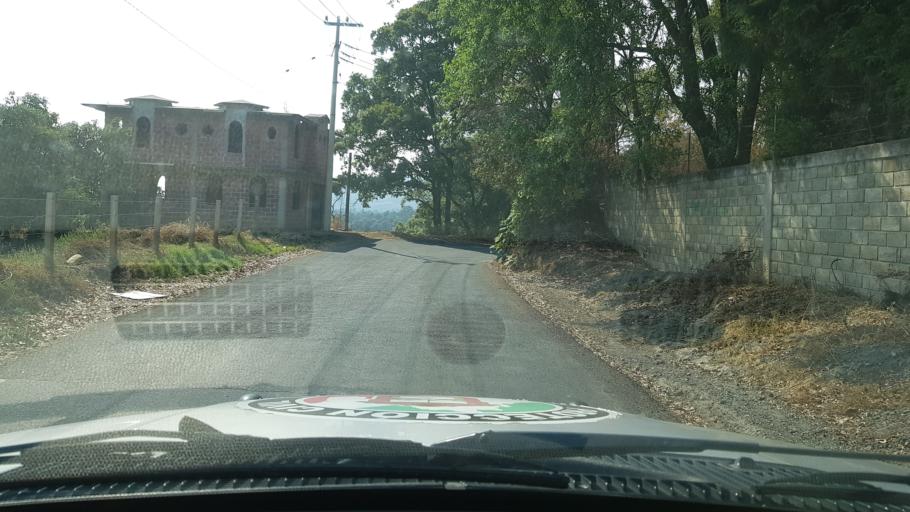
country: MX
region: Mexico
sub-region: Ozumba
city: San Jose Tlacotitlan
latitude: 18.9872
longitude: -98.8180
